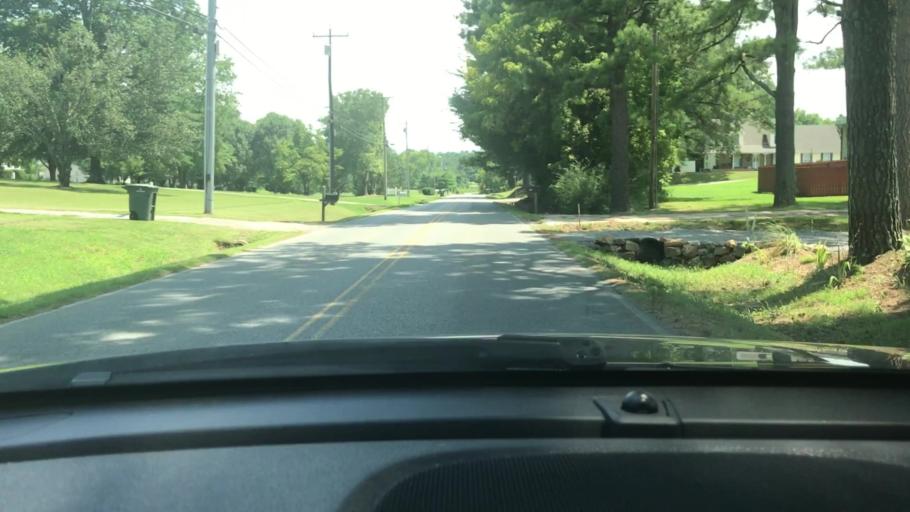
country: US
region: Tennessee
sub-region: Sumner County
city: White House
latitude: 36.4644
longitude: -86.6480
